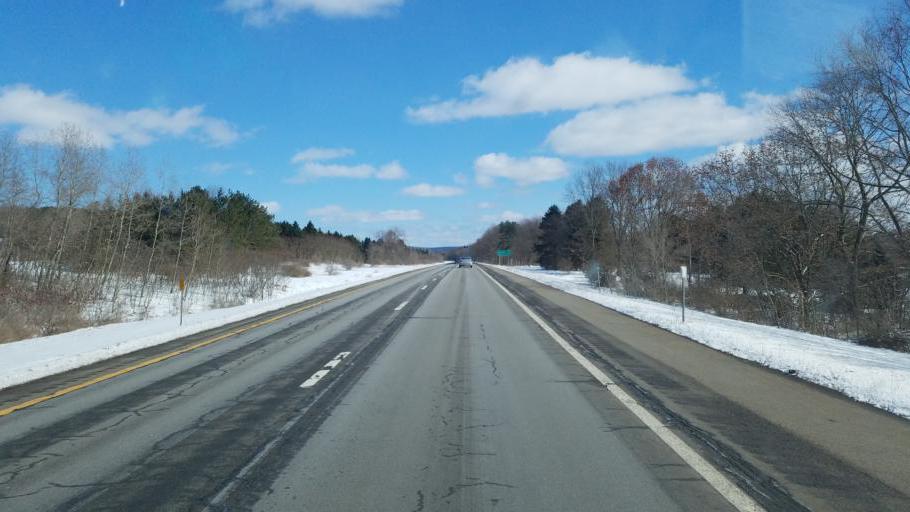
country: US
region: New York
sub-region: Chautauqua County
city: Falconer
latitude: 42.1365
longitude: -79.1571
